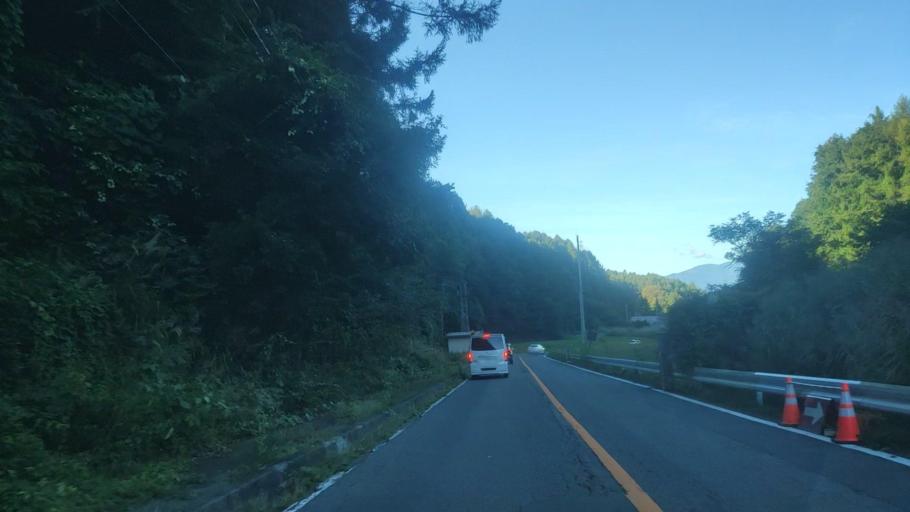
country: JP
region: Nagano
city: Kamimaruko
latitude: 36.2333
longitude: 138.2998
